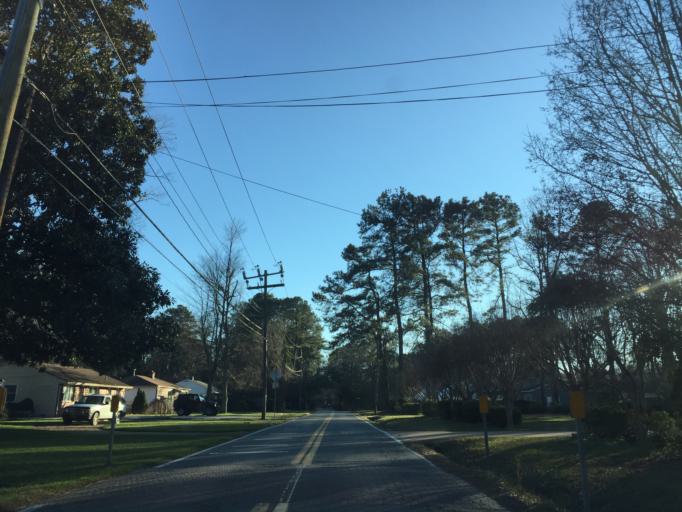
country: US
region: Virginia
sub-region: City of Newport News
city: Newport News
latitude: 37.0747
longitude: -76.5086
